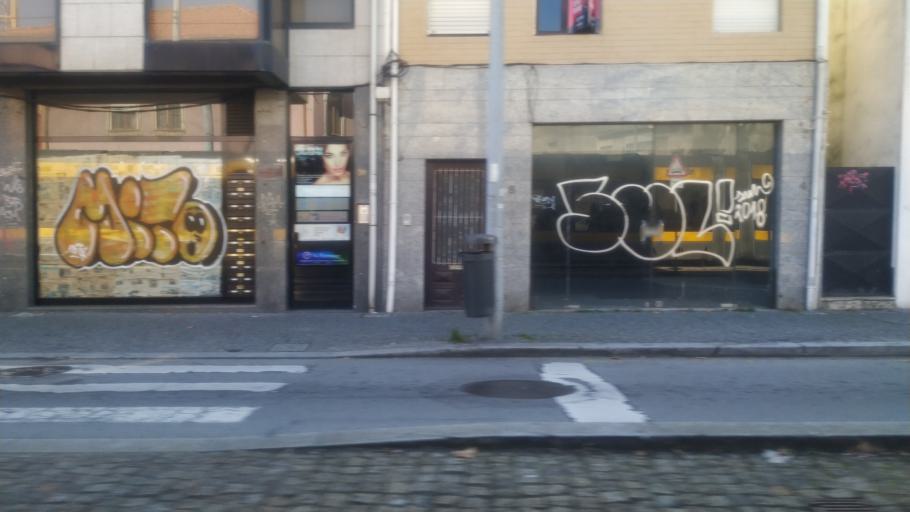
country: PT
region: Porto
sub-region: Matosinhos
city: Matosinhos
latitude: 41.1798
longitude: -8.6791
